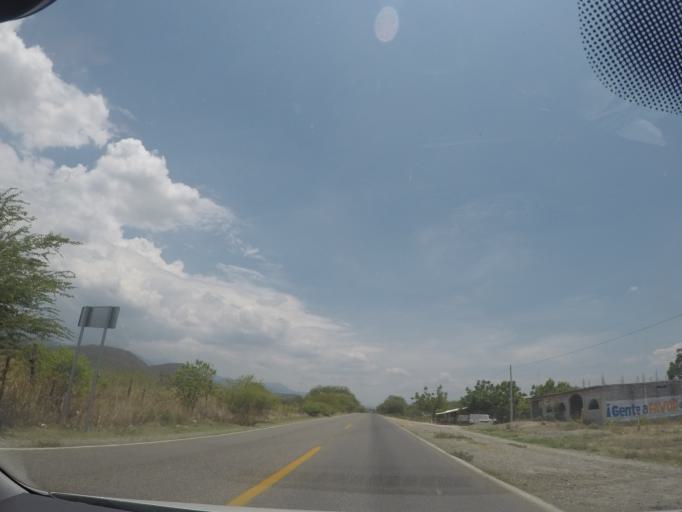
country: MX
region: Oaxaca
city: Santa Maria Jalapa del Marques
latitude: 16.4370
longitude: -95.5256
